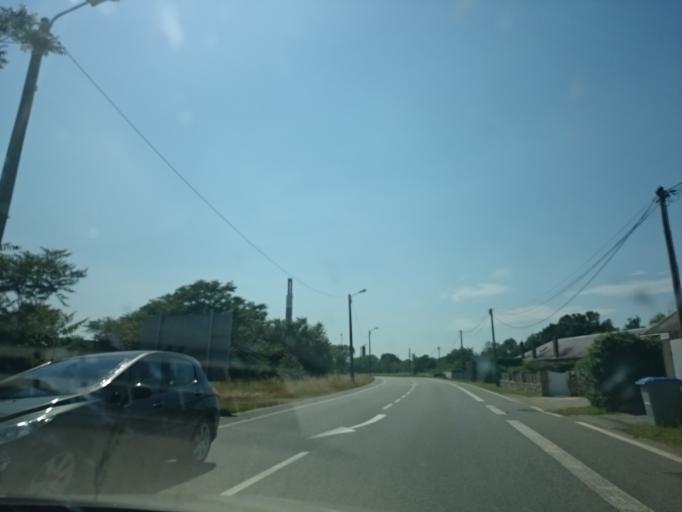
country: FR
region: Pays de la Loire
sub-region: Departement de la Loire-Atlantique
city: Coueron
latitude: 47.2097
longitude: -1.7029
